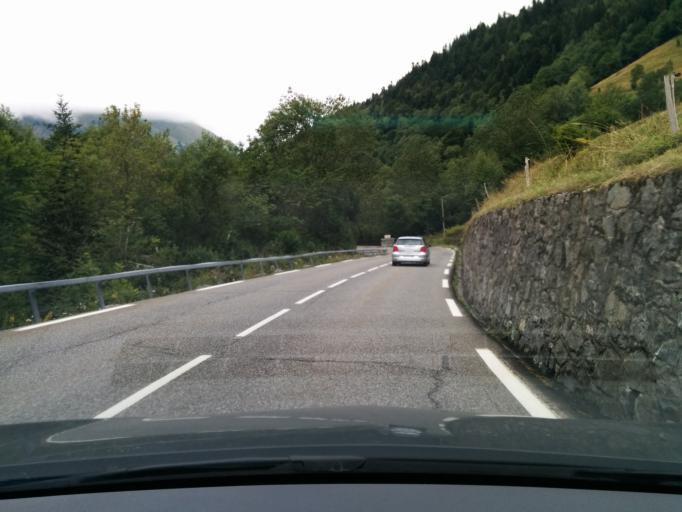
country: FR
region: Midi-Pyrenees
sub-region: Departement des Hautes-Pyrenees
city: Saint-Lary-Soulan
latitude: 42.7825
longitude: 0.2039
